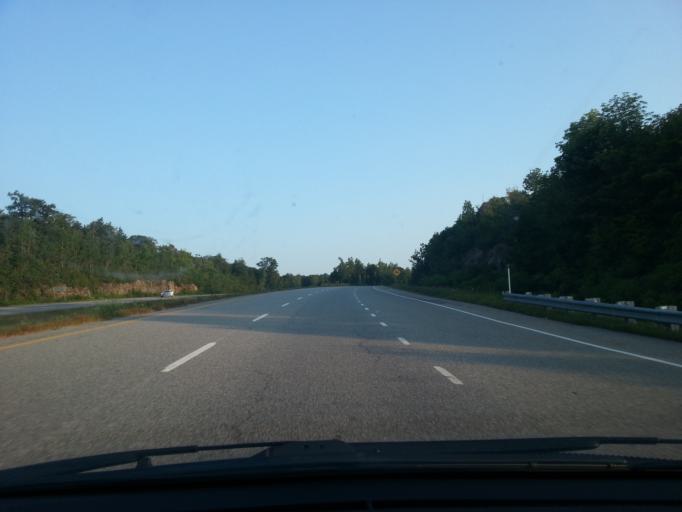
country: CA
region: Quebec
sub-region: Outaouais
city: Gatineau
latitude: 45.5184
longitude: -75.8156
